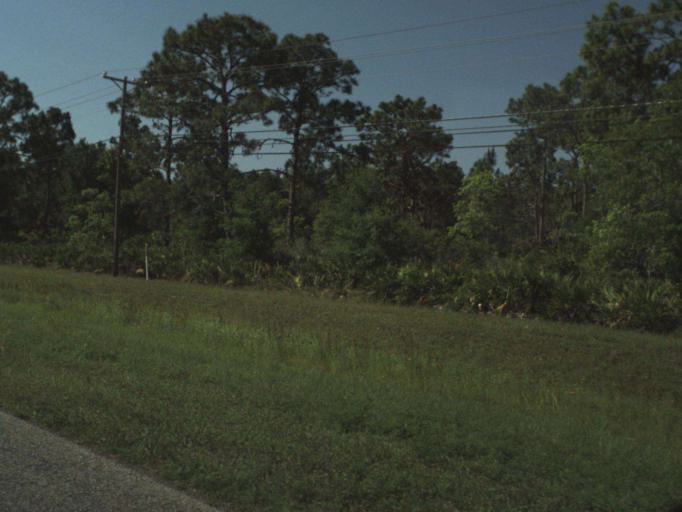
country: US
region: Florida
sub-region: Orange County
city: Bithlo
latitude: 28.5336
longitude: -81.0781
